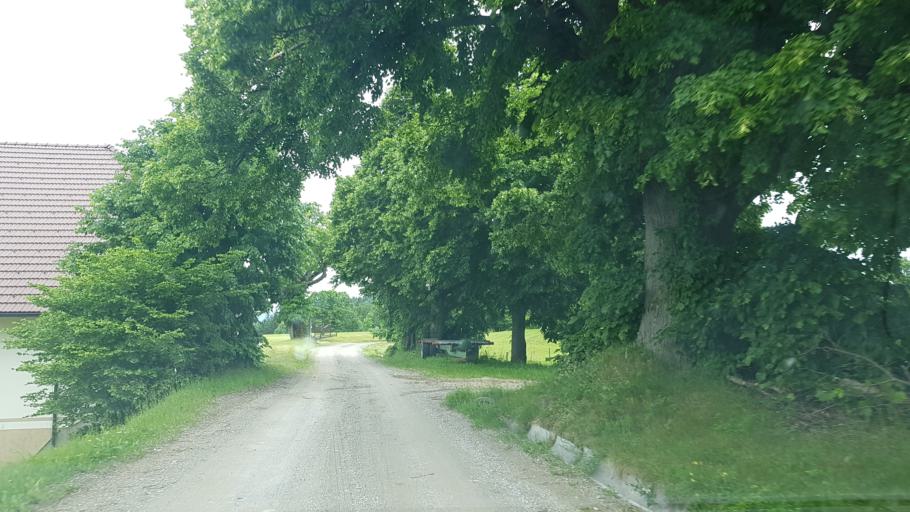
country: SI
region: Dobrna
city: Dobrna
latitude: 46.3694
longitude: 15.2480
